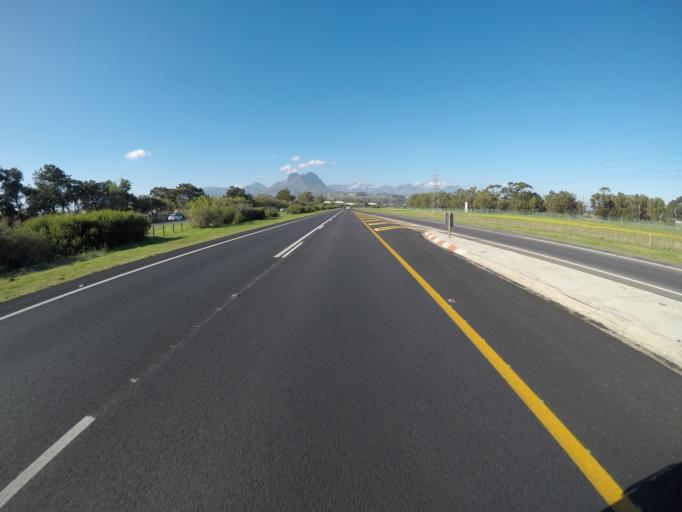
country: ZA
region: Western Cape
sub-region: Cape Winelands District Municipality
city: Stellenbosch
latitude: -34.0592
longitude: 18.7847
